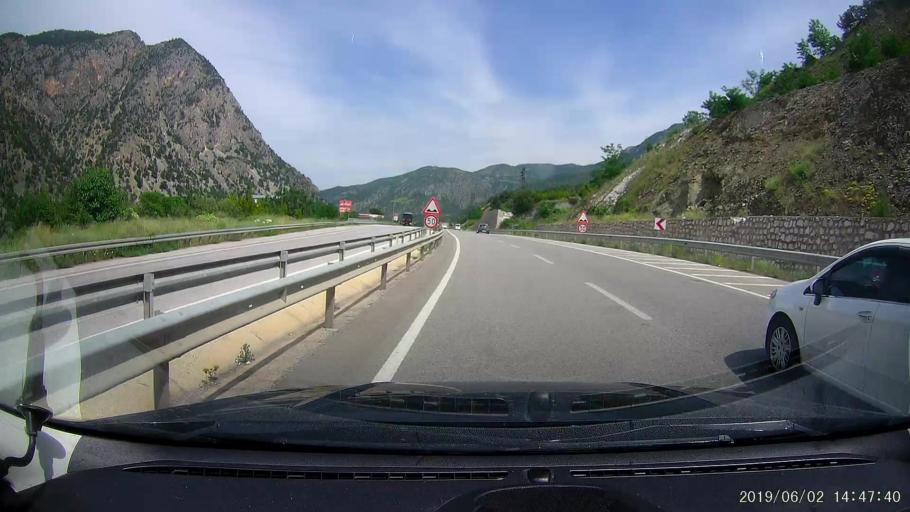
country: TR
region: Corum
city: Hacihamza
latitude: 41.0662
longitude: 34.4651
